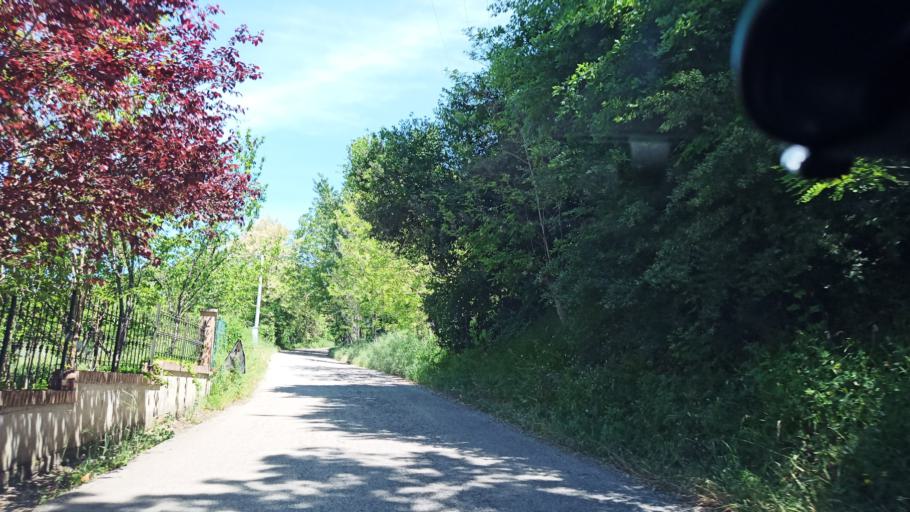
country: IT
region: Latium
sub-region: Provincia di Rieti
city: Torri in Sabina
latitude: 42.3573
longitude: 12.6348
